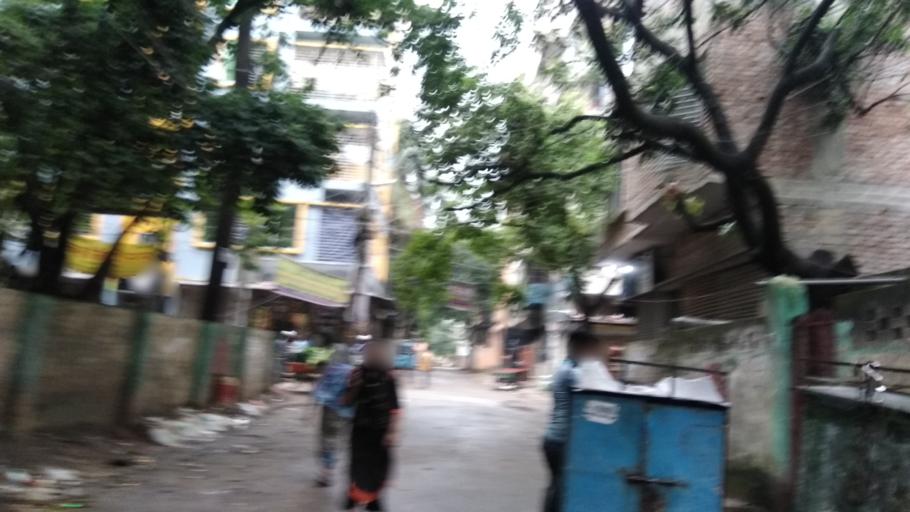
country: BD
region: Dhaka
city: Tungi
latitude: 23.8281
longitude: 90.3705
